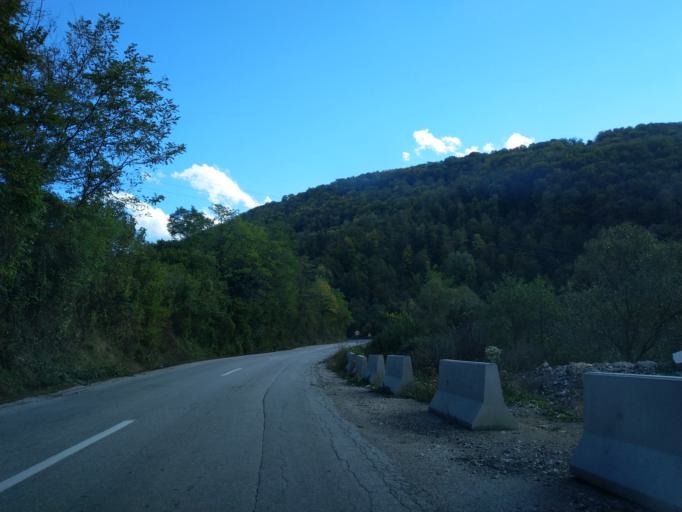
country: RS
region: Central Serbia
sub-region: Zlatiborski Okrug
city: Uzice
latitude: 43.8810
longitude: 19.7788
